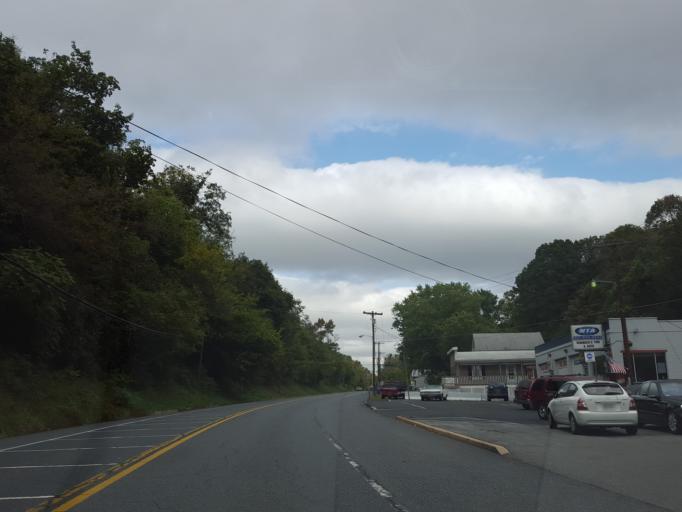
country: US
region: Maryland
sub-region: Frederick County
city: Brunswick
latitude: 39.3156
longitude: -77.6282
